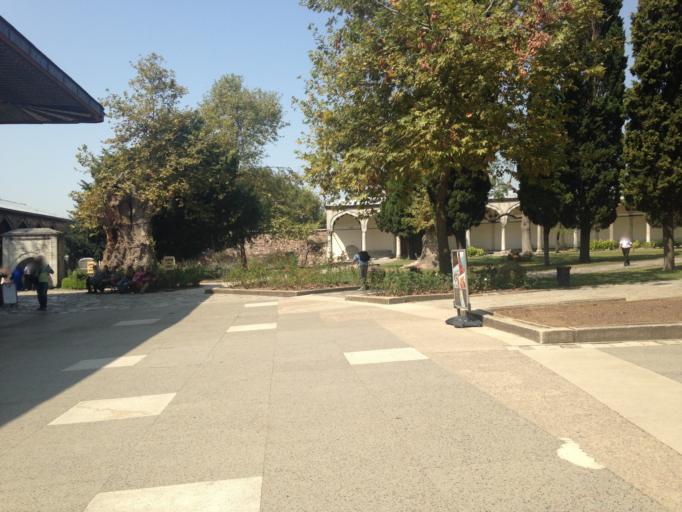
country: TR
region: Istanbul
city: Eminoenue
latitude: 41.0116
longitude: 28.9834
